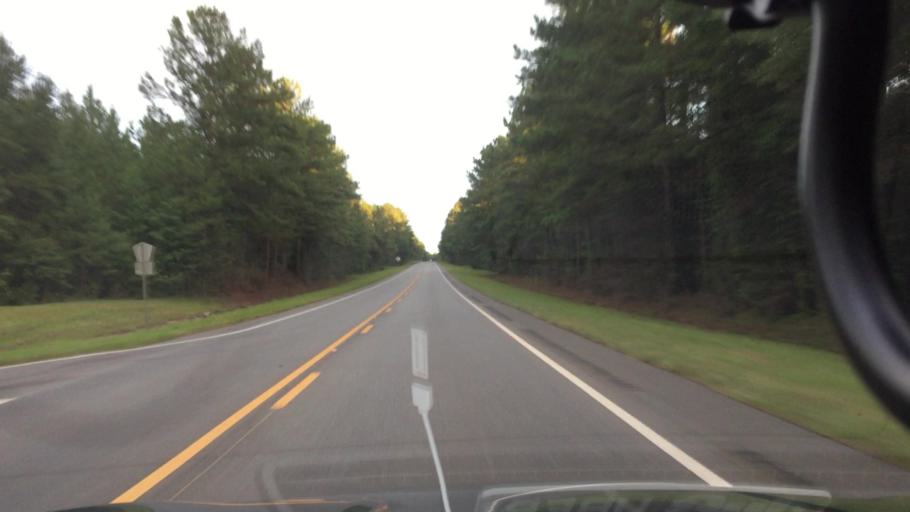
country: US
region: Alabama
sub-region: Pike County
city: Brundidge
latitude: 31.5839
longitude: -85.9367
